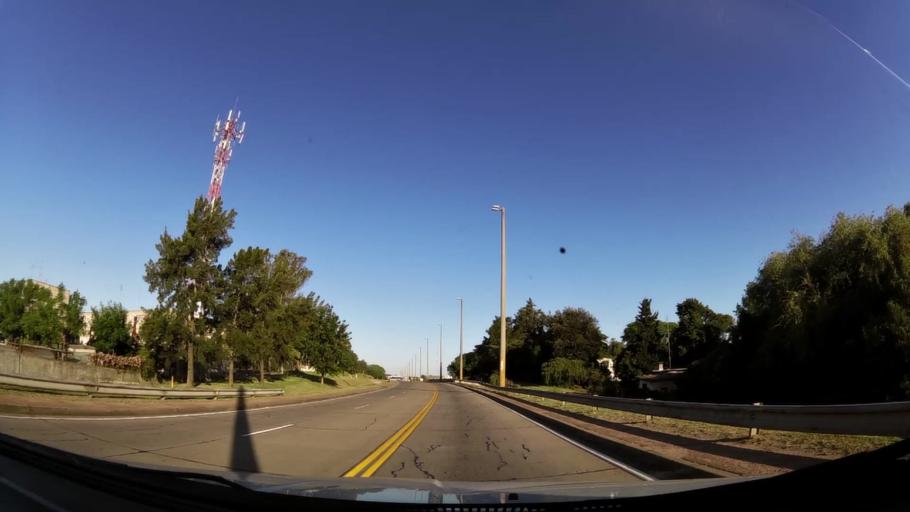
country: UY
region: Canelones
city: La Paz
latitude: -34.8272
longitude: -56.2419
